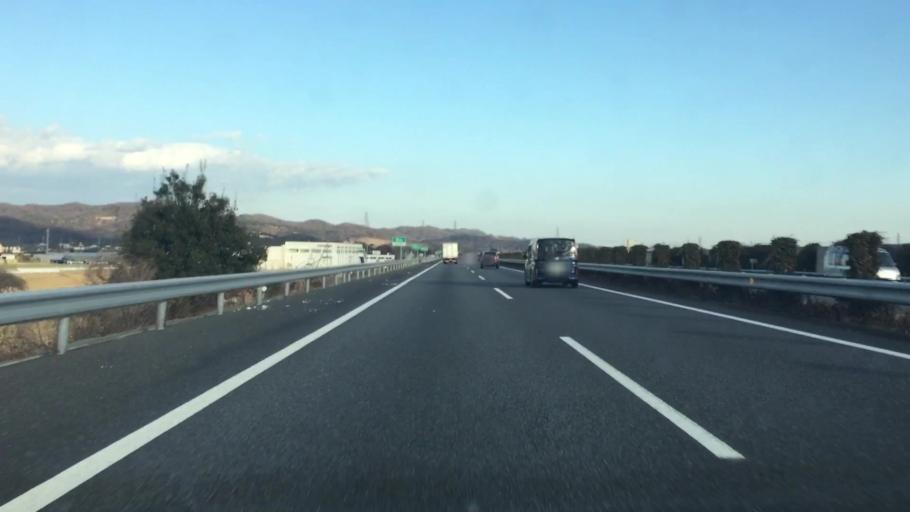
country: JP
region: Gunma
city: Kiryu
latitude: 36.3463
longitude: 139.3048
